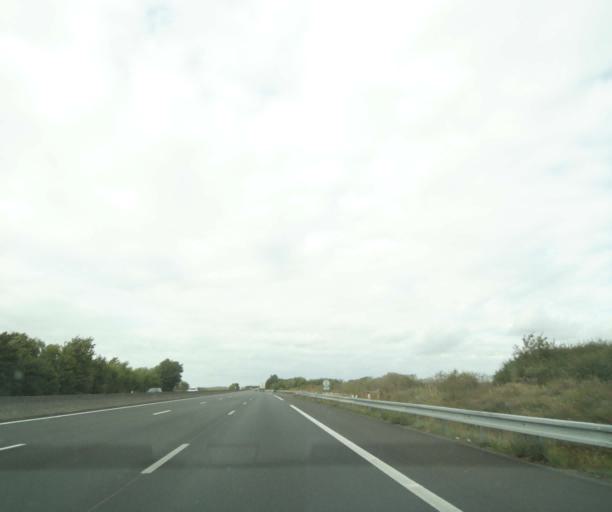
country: FR
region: Centre
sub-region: Departement d'Eure-et-Loir
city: Janville
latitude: 48.2444
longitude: 1.8515
